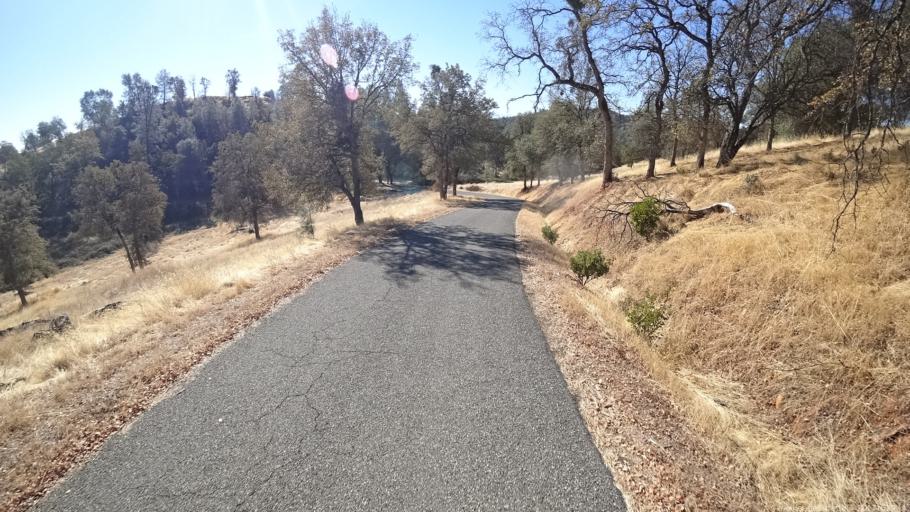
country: US
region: California
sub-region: Shasta County
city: Shasta
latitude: 40.4778
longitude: -122.6222
